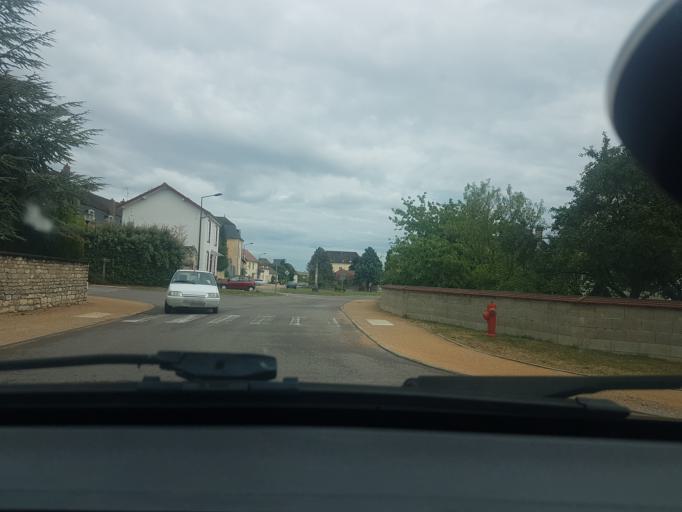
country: FR
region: Bourgogne
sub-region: Departement de Saone-et-Loire
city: Fontaines
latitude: 46.8531
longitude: 4.7671
